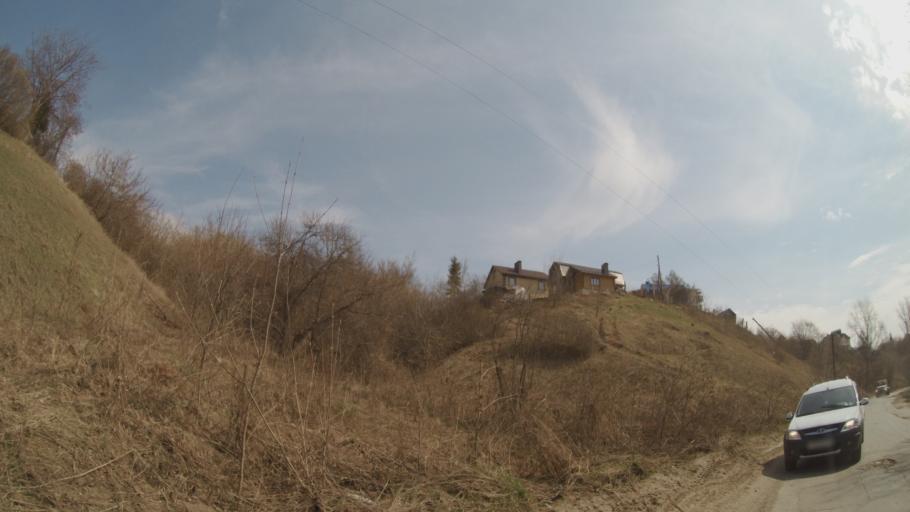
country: RU
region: Nizjnij Novgorod
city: Vyyezdnoye
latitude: 55.3920
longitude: 43.8071
